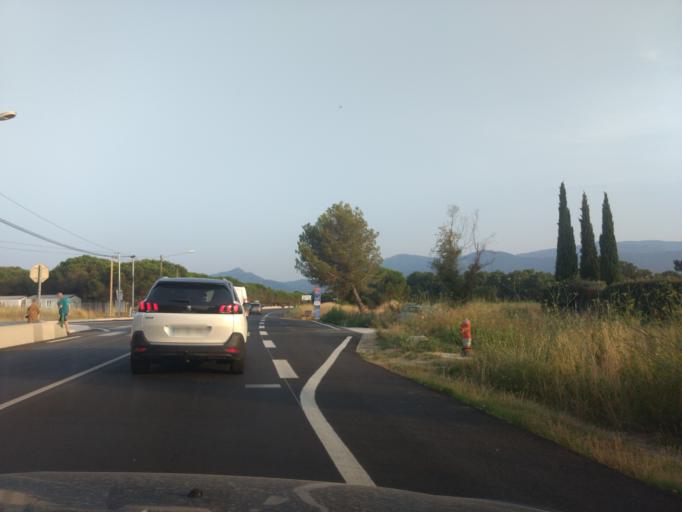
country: FR
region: Languedoc-Roussillon
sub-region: Departement des Pyrenees-Orientales
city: Argelers
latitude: 42.5703
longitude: 3.0408
